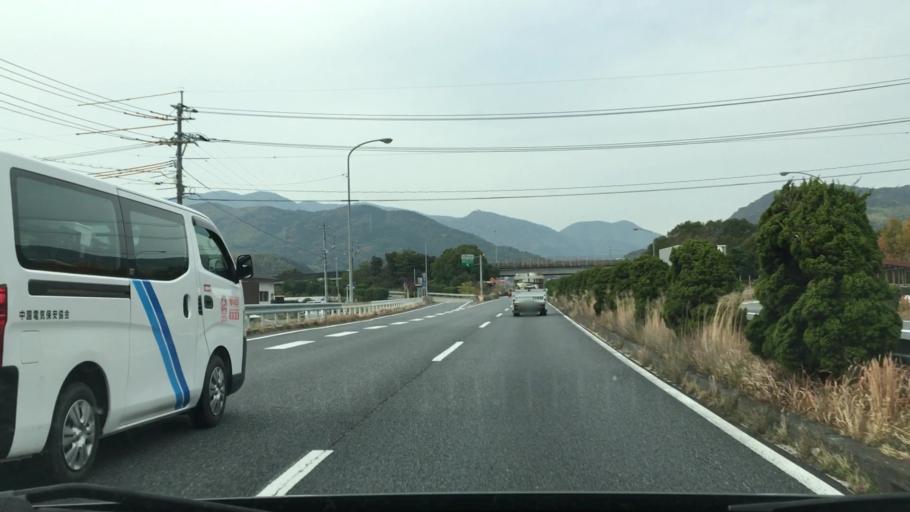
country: JP
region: Yamaguchi
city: Tokuyama
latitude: 34.0699
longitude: 131.6963
